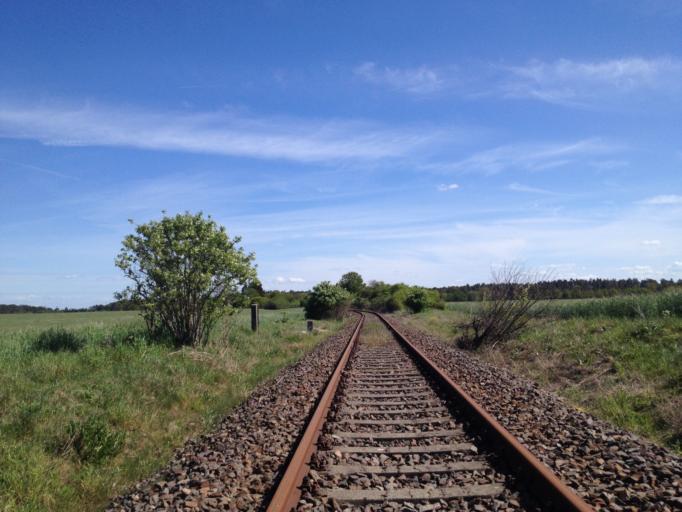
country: DE
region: Brandenburg
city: Templin
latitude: 53.1180
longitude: 13.4550
